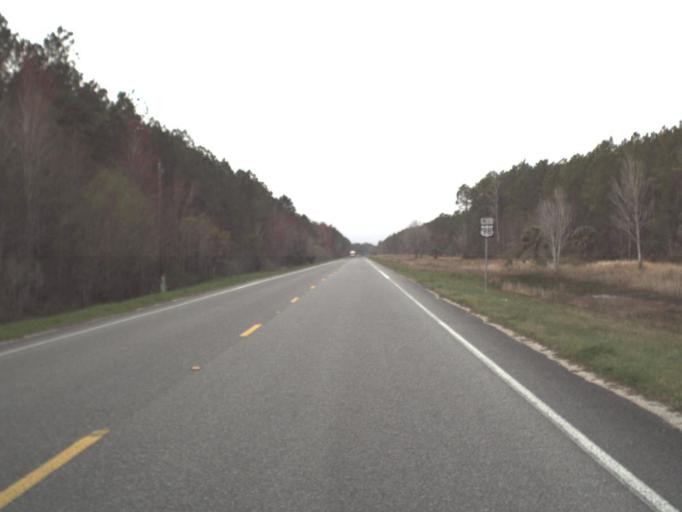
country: US
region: Florida
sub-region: Leon County
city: Woodville
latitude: 30.1945
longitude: -84.1326
